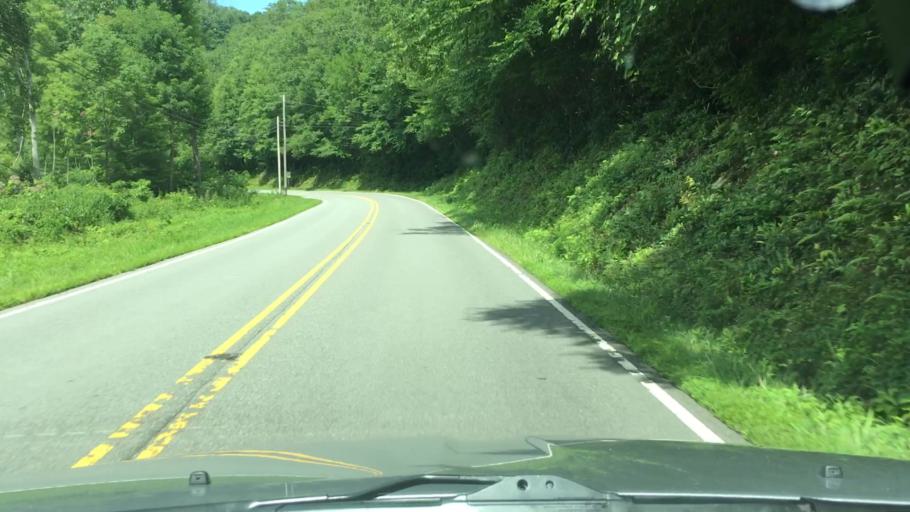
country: US
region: North Carolina
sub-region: Yancey County
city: Burnsville
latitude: 35.7924
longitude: -82.2022
